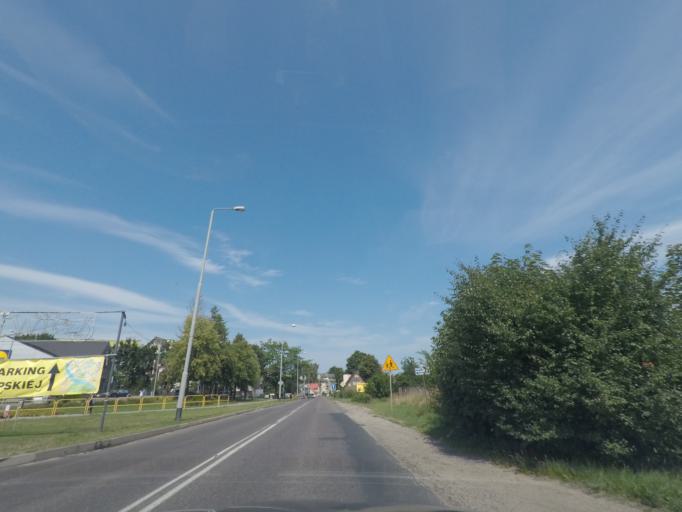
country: PL
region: Pomeranian Voivodeship
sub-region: Powiat slupski
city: Ustka
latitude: 54.5753
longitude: 16.8528
